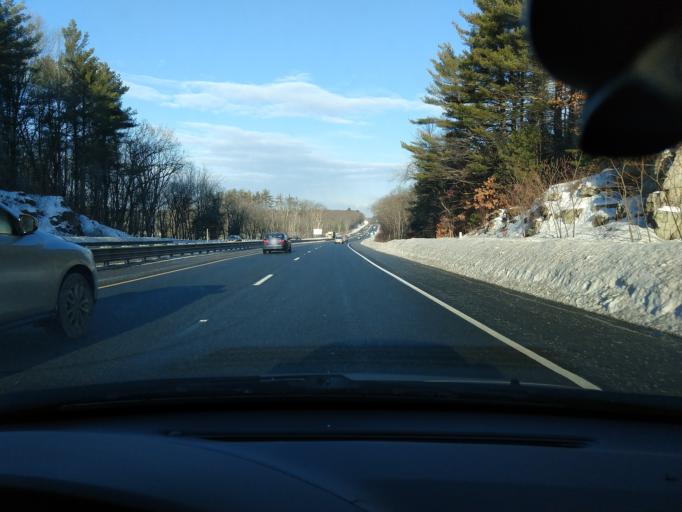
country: US
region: Massachusetts
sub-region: Middlesex County
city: Littleton Common
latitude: 42.5062
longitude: -71.4851
